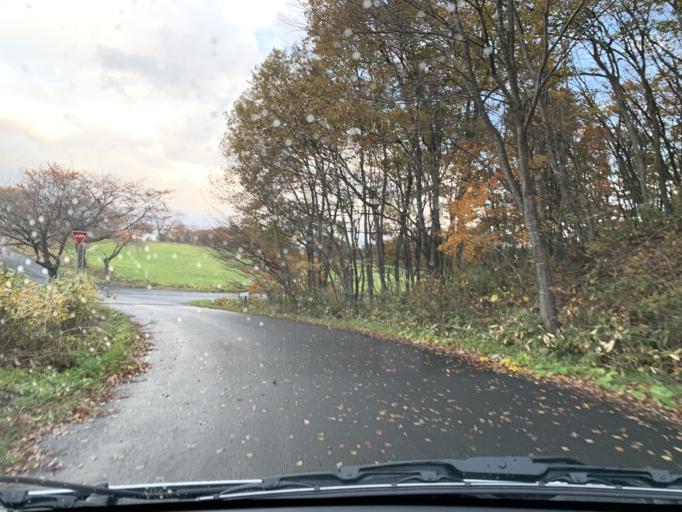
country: JP
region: Iwate
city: Mizusawa
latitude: 39.0744
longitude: 141.0294
